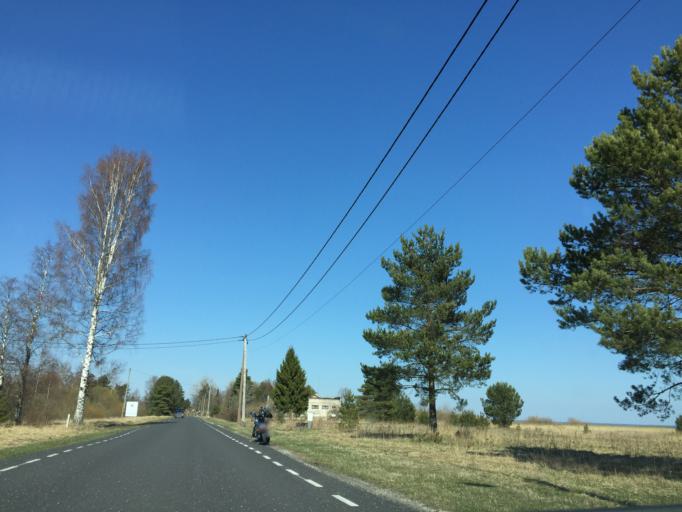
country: EE
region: Jogevamaa
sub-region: Mustvee linn
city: Mustvee
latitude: 58.8631
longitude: 26.9521
